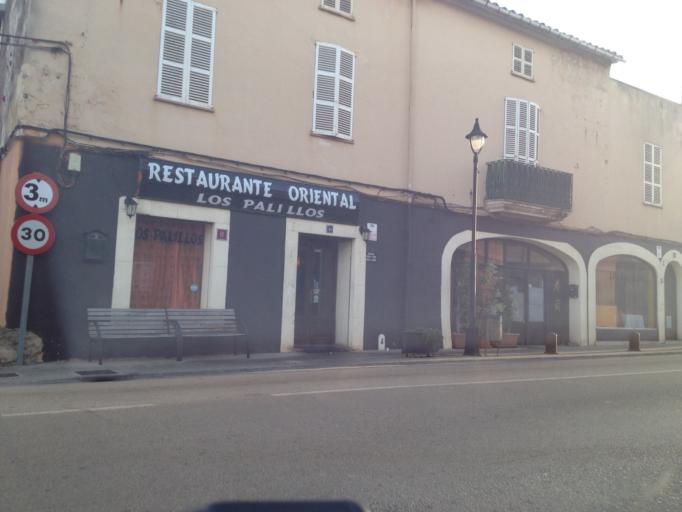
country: ES
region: Balearic Islands
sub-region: Illes Balears
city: Santa Maria del Cami
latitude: 39.6500
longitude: 2.7708
